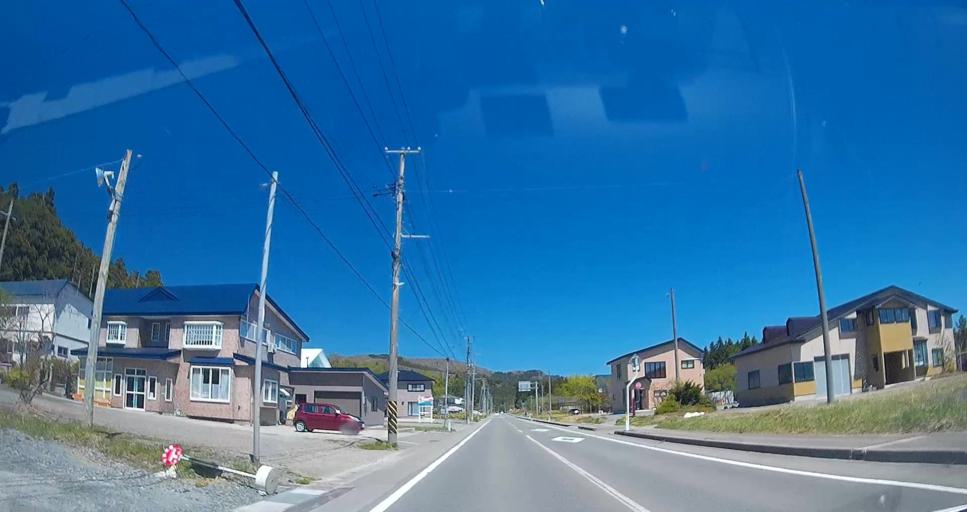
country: JP
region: Aomori
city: Mutsu
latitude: 41.0823
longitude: 141.3859
